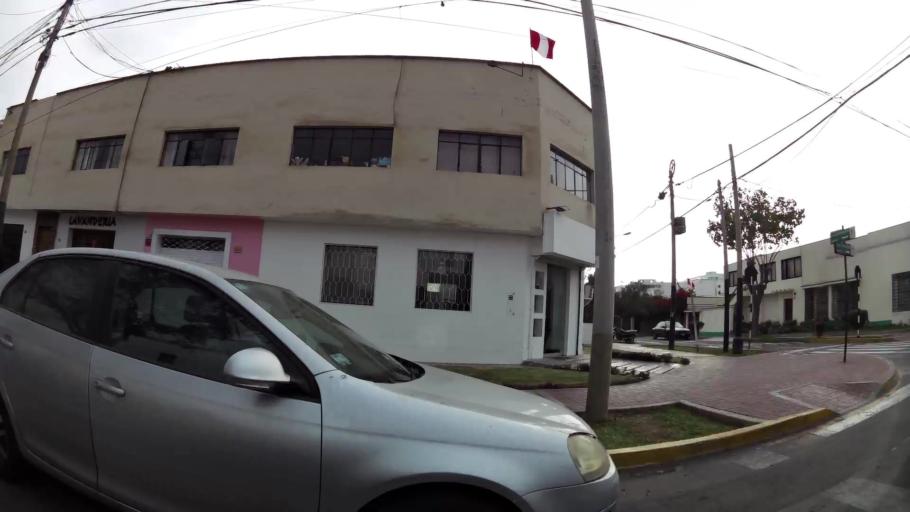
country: PE
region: Lima
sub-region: Lima
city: San Isidro
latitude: -12.1012
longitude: -77.0539
